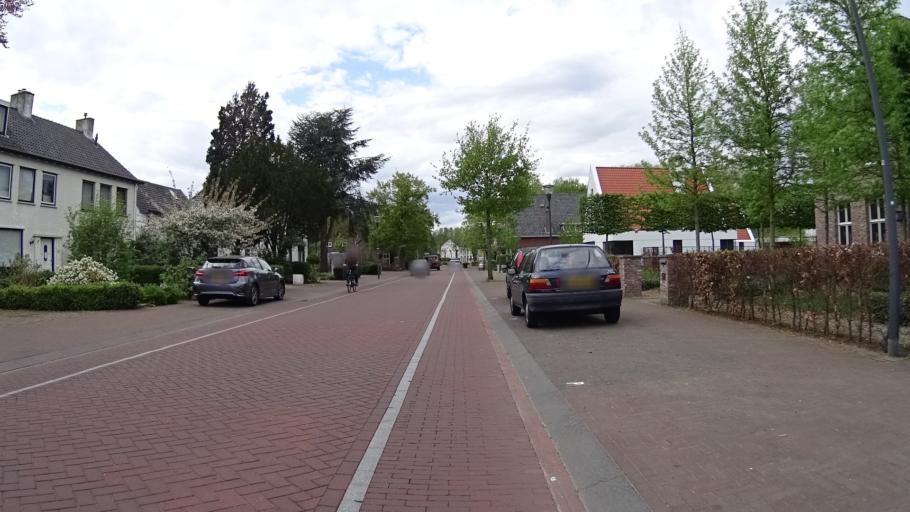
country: NL
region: North Brabant
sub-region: Gemeente Nuenen, Gerwen en Nederwetten
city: Nuenen
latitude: 51.4782
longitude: 5.5508
